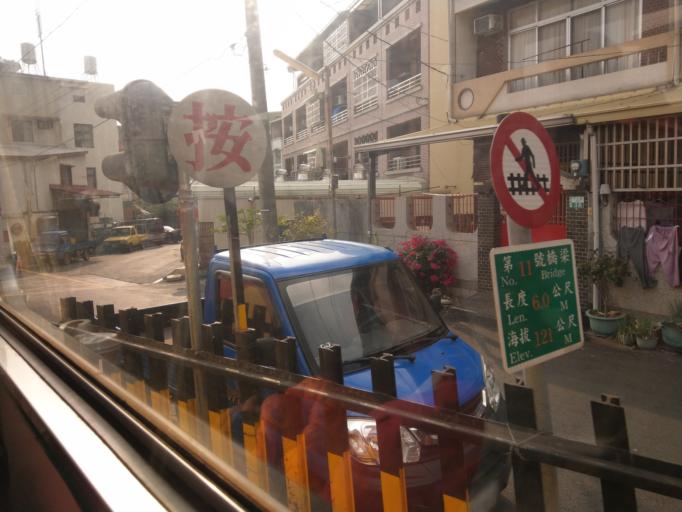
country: TW
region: Taiwan
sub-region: Chiayi
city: Jiayi Shi
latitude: 23.5235
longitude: 120.5502
